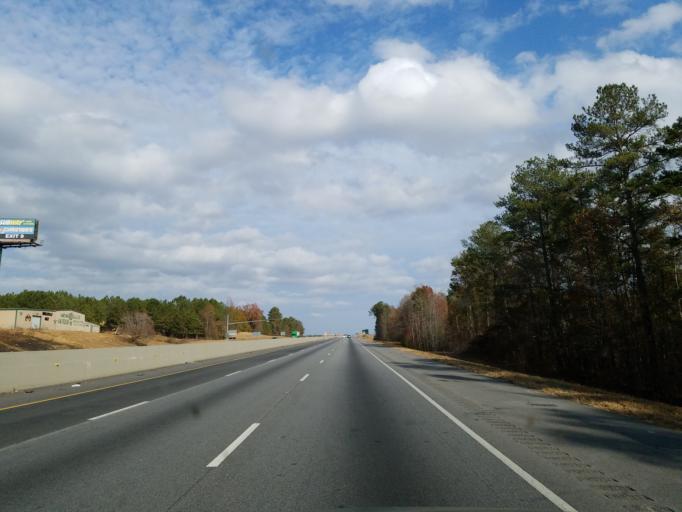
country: US
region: Alabama
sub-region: Cleburne County
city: Heflin
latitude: 33.6492
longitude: -85.4230
